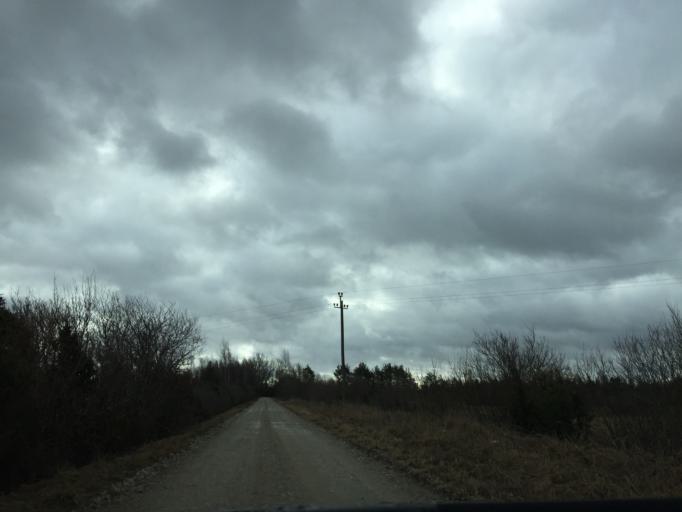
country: EE
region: Laeaene
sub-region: Haapsalu linn
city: Haapsalu
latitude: 58.6846
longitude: 23.5092
